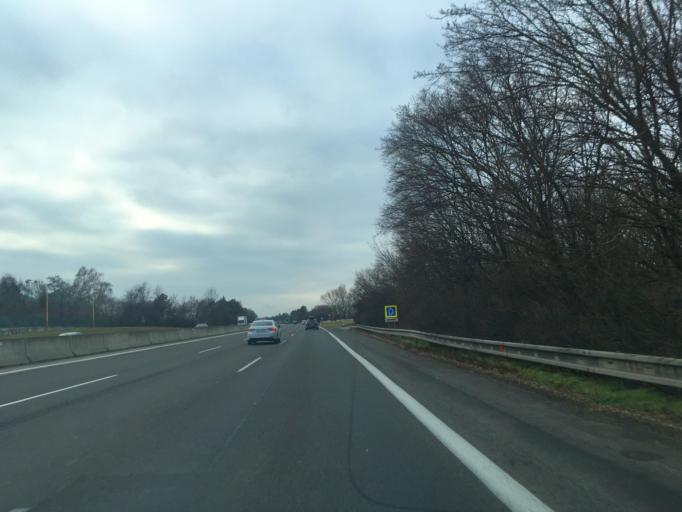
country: SK
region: Bratislavsky
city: Senec
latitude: 48.2446
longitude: 17.3907
